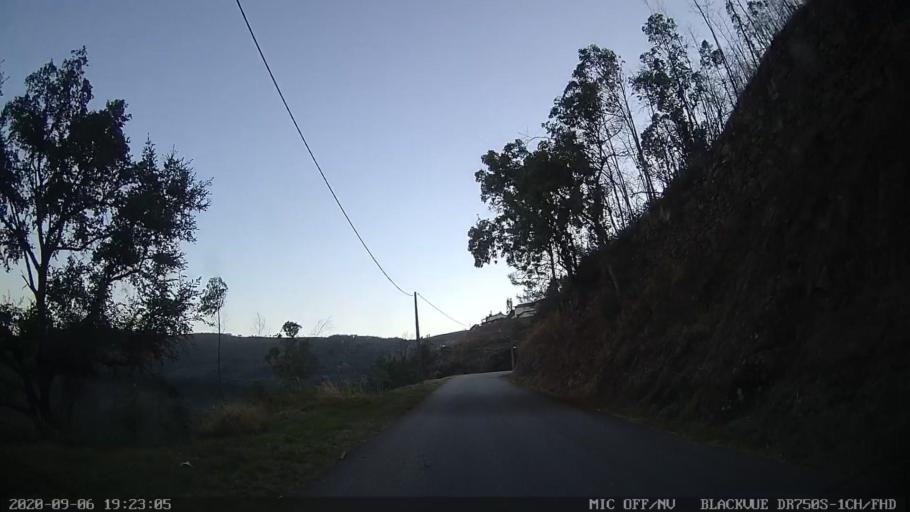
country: PT
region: Vila Real
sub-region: Mesao Frio
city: Mesao Frio
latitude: 41.1866
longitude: -7.9243
